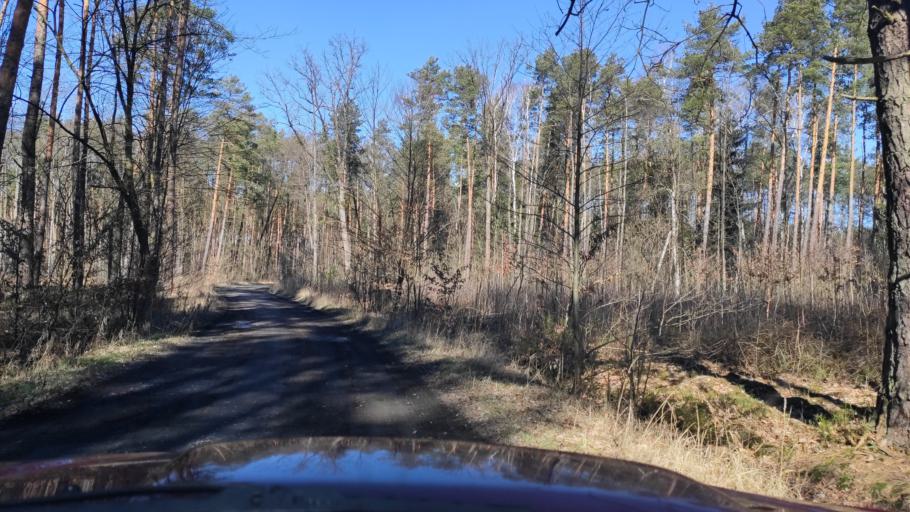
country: PL
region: Masovian Voivodeship
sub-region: Powiat kozienicki
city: Garbatka-Letnisko
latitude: 51.4447
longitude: 21.5357
